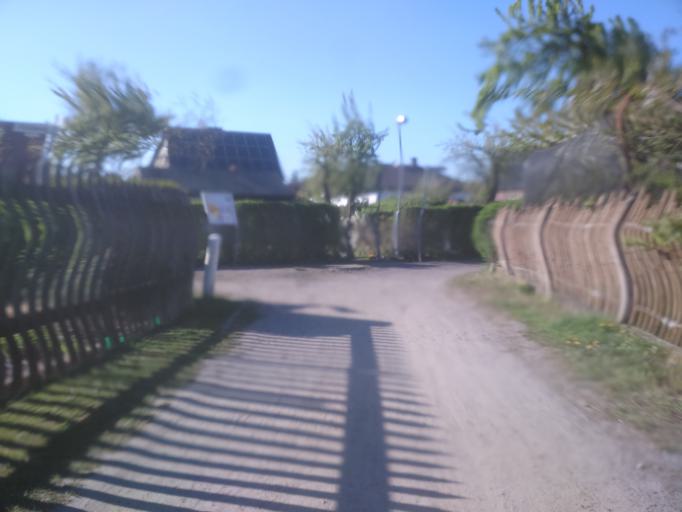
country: DE
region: Berlin
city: Neu-Hohenschoenhausen
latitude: 52.5578
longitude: 13.5080
